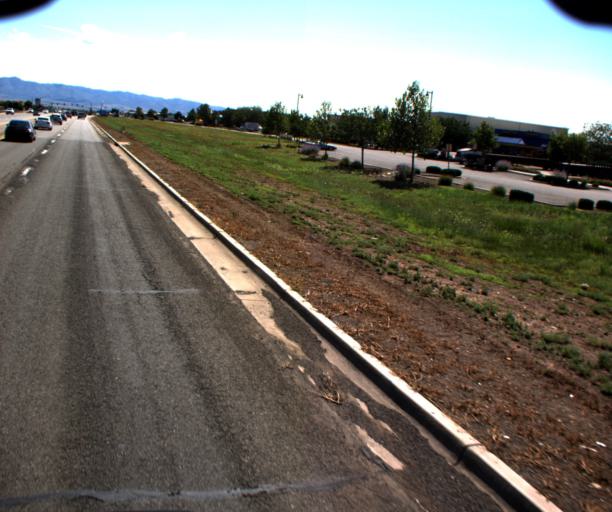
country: US
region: Arizona
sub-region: Yavapai County
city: Prescott Valley
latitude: 34.5821
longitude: -112.3475
